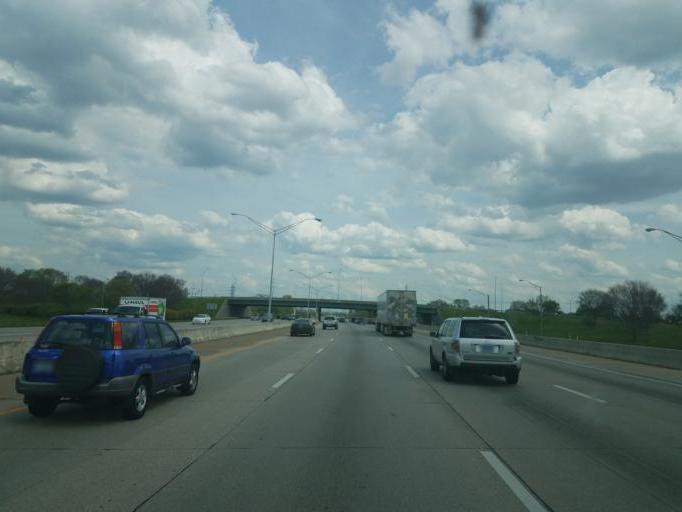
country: US
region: Kentucky
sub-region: Jefferson County
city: Saint Regis Park
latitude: 38.2273
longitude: -85.6387
